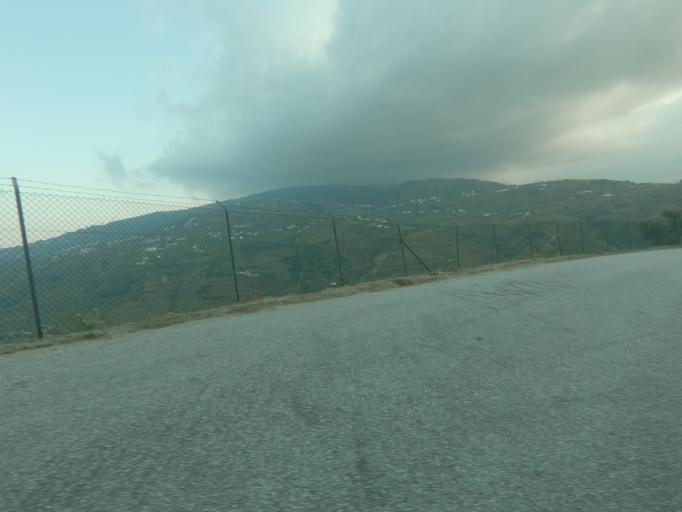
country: PT
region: Vila Real
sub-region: Mesao Frio
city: Mesao Frio
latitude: 41.1614
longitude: -7.8510
